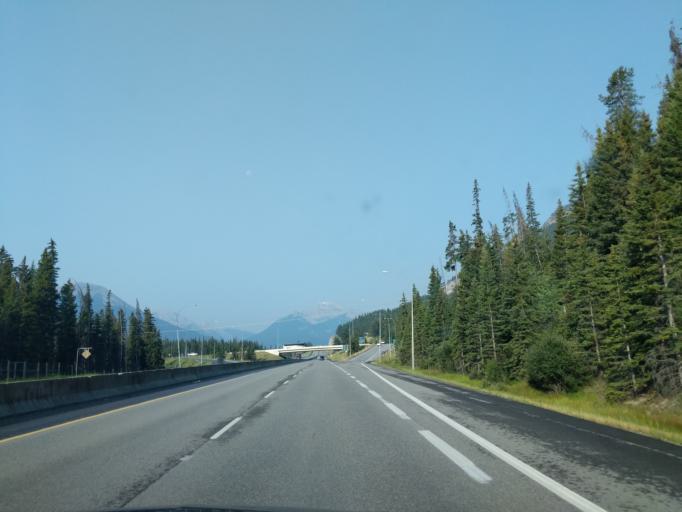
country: CA
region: Alberta
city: Banff
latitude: 51.1894
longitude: -115.5791
